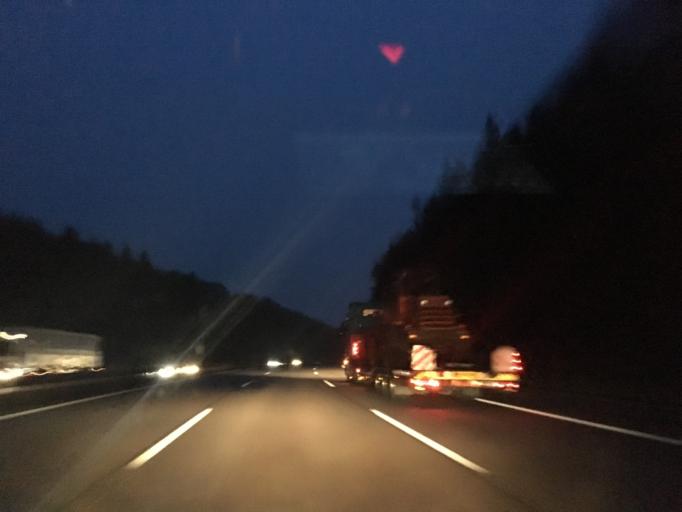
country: DE
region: Rheinland-Pfalz
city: Oberhaid
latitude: 50.5027
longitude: 7.7296
